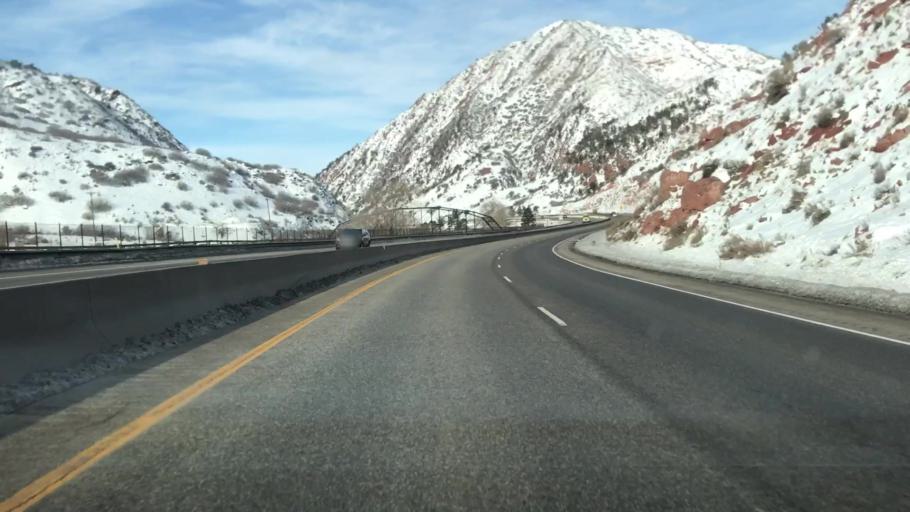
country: US
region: Colorado
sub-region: Garfield County
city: Glenwood Springs
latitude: 39.5594
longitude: -107.4038
